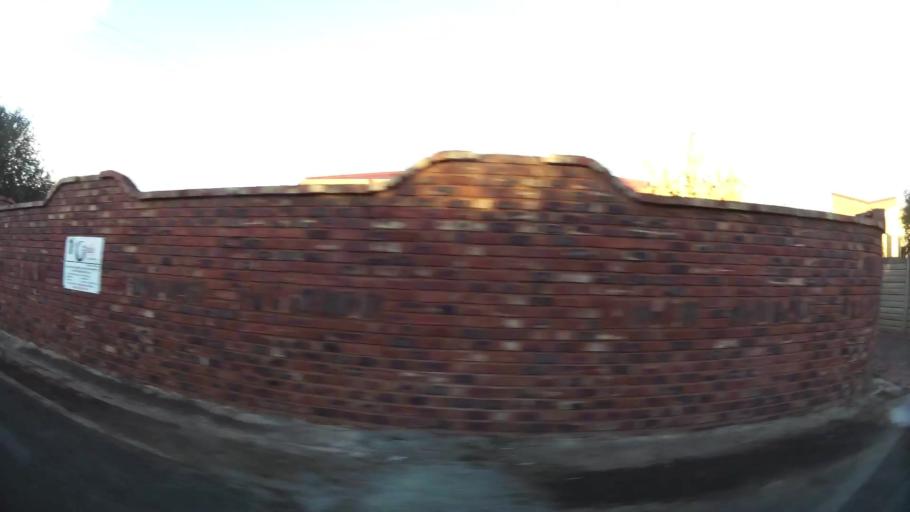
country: ZA
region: North-West
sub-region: Dr Kenneth Kaunda District Municipality
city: Potchefstroom
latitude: -26.7197
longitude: 27.0915
